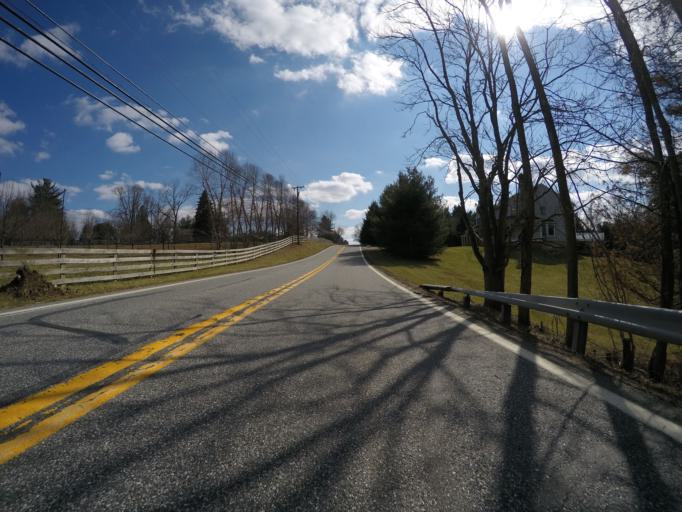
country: US
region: Maryland
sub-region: Baltimore County
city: Cockeysville
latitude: 39.4665
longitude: -76.7003
